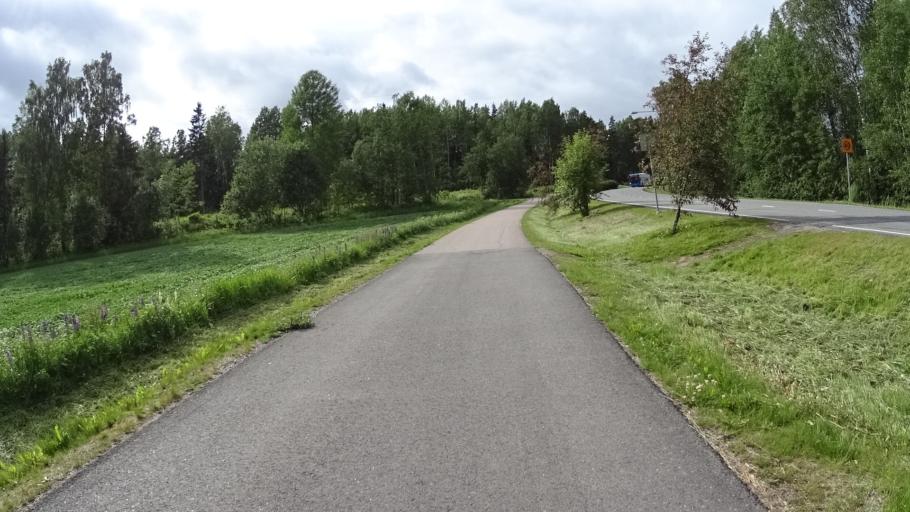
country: FI
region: Uusimaa
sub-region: Helsinki
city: Kilo
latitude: 60.2505
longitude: 24.8009
